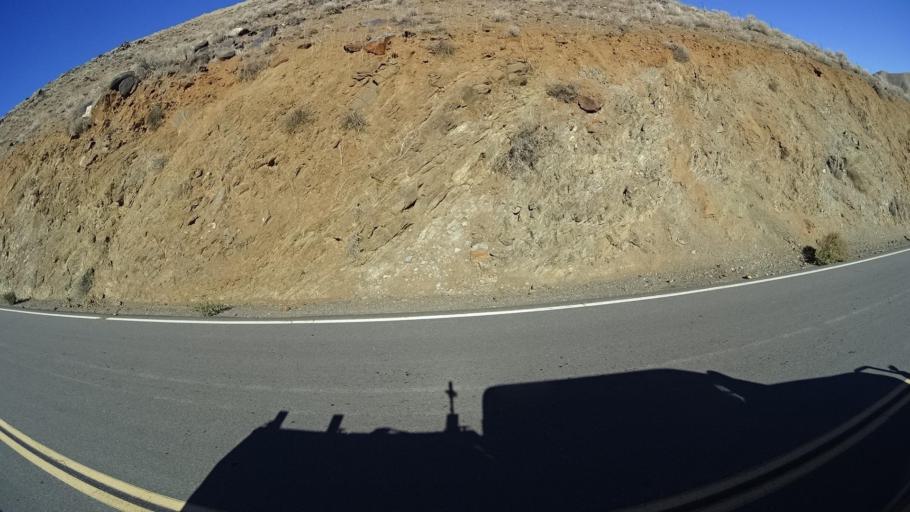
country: US
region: California
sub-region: Kern County
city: Wofford Heights
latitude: 35.6826
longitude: -118.3817
